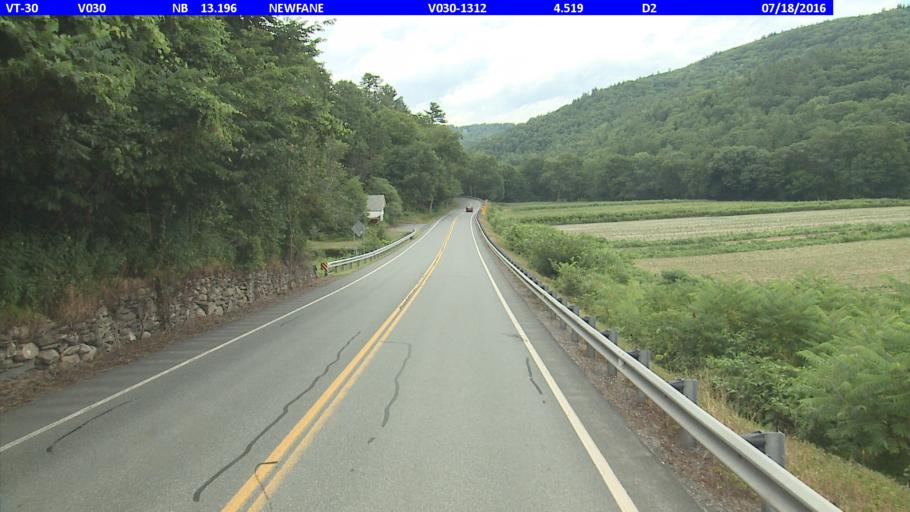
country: US
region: Vermont
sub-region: Windham County
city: Newfane
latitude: 43.0059
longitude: -72.6447
